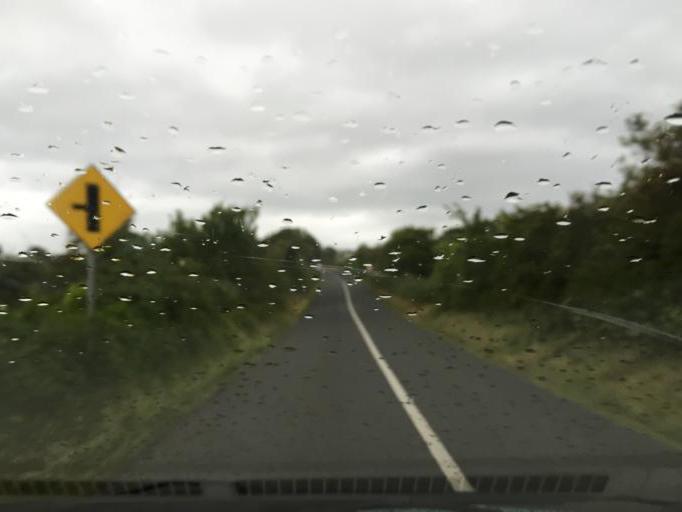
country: IE
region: Connaught
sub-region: Sligo
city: Strandhill
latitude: 54.2568
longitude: -8.5972
